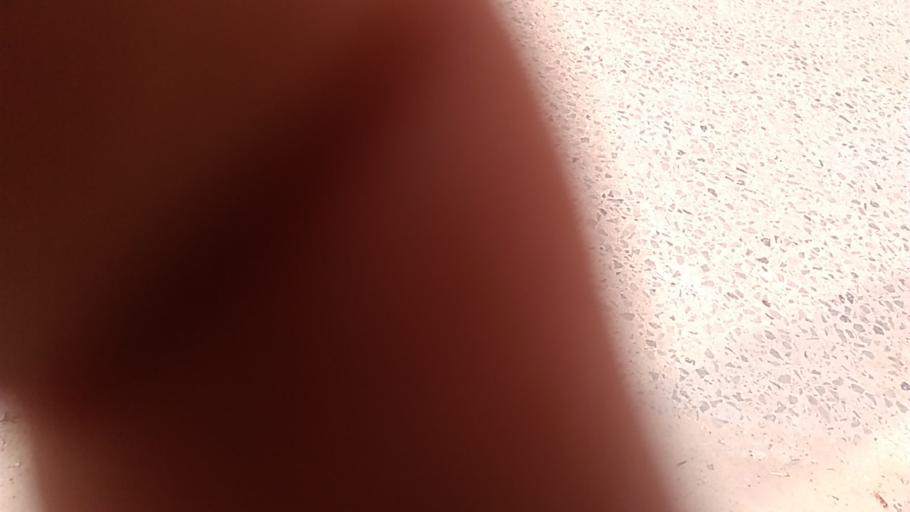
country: IN
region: West Bengal
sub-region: Nadia
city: Navadwip
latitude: 23.4161
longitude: 88.3838
